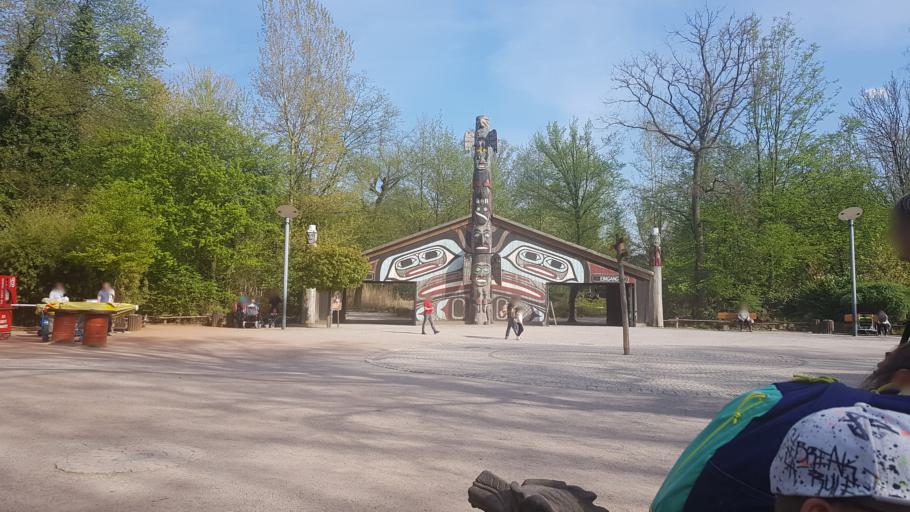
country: DE
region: North Rhine-Westphalia
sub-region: Regierungsbezirk Munster
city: Gelsenkirchen
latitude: 51.5433
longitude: 7.1111
